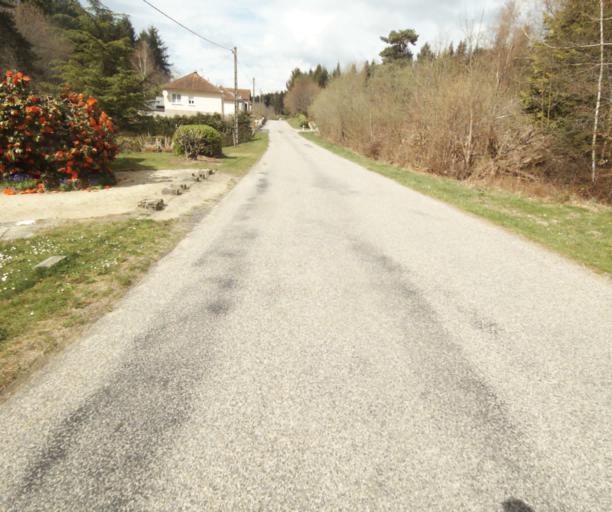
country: FR
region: Limousin
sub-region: Departement de la Correze
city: Correze
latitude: 45.2688
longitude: 1.9777
